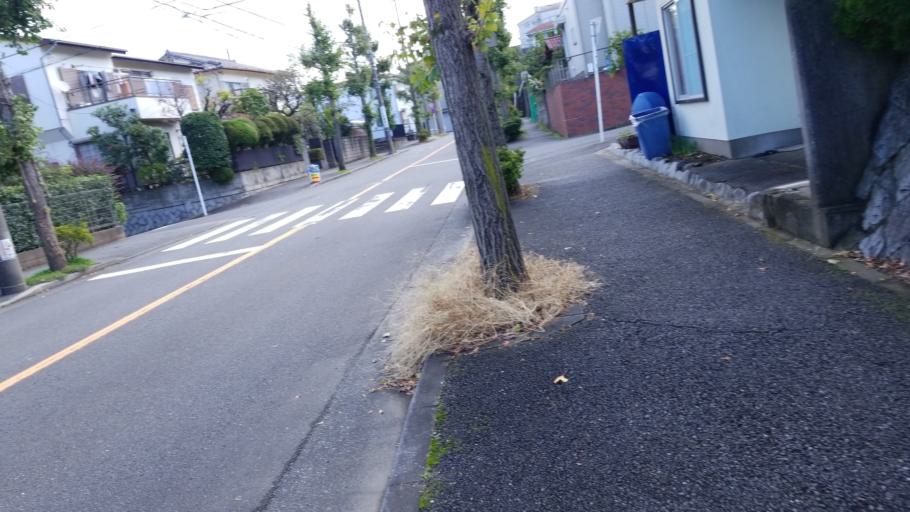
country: JP
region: Tokyo
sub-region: Machida-shi
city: Machida
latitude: 35.5882
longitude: 139.5007
